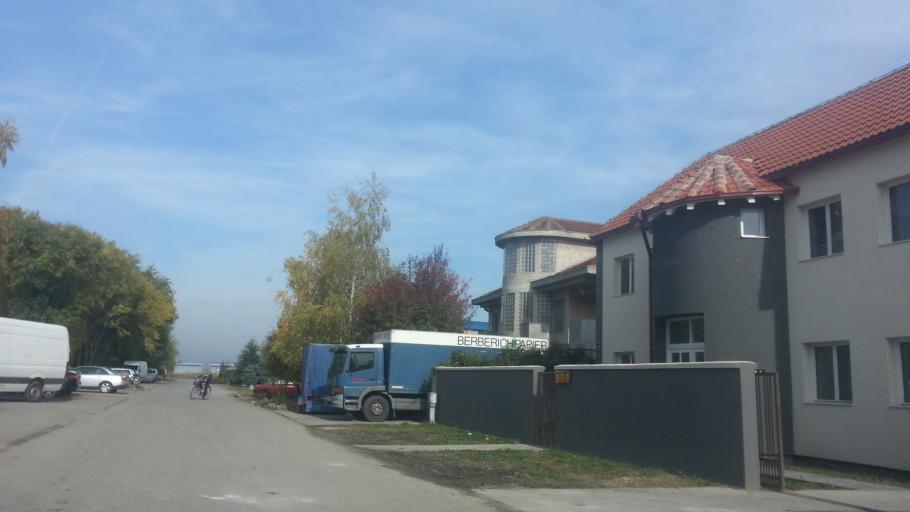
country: RS
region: Autonomna Pokrajina Vojvodina
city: Nova Pazova
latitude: 44.9479
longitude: 20.2034
